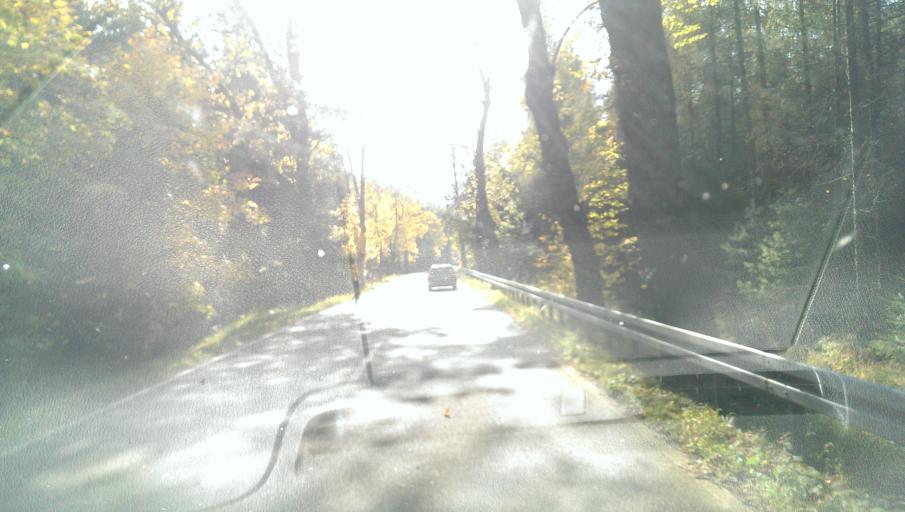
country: DE
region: Saxony
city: Dohma
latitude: 50.8393
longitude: 13.9652
